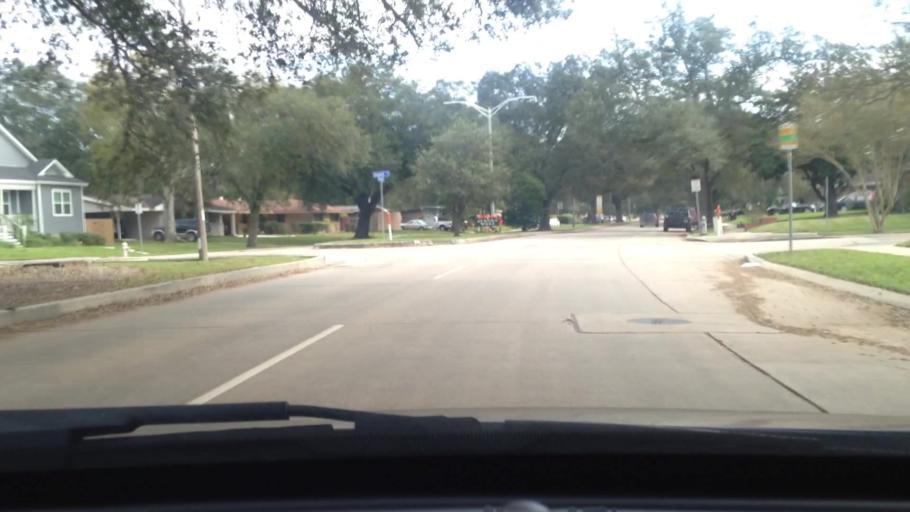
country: US
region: Louisiana
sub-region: Saint Bernard Parish
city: Arabi
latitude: 29.9235
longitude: -90.0020
